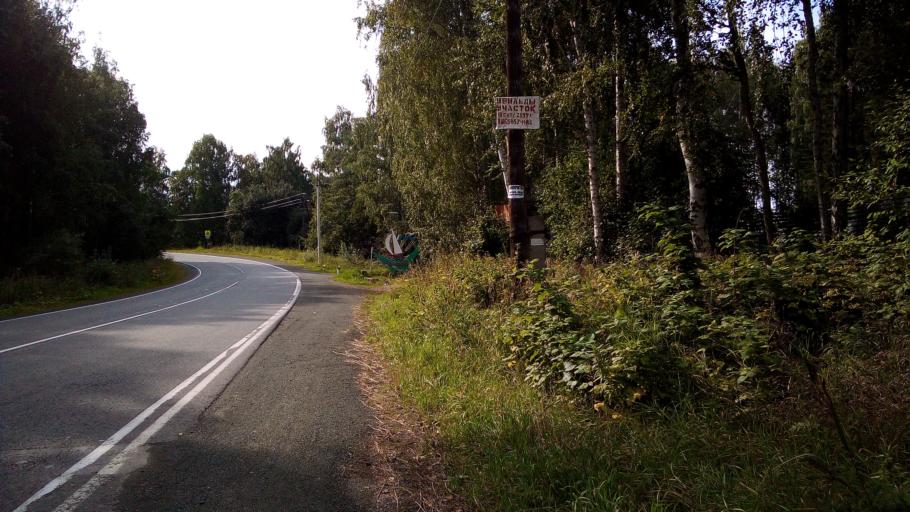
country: RU
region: Chelyabinsk
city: Tayginka
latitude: 55.4747
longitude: 60.4906
